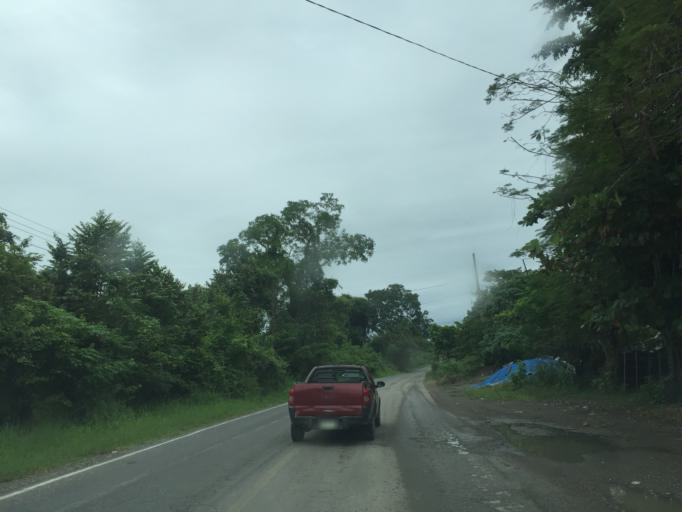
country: MX
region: Veracruz
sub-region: Papantla
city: El Chote
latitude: 20.4379
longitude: -97.3833
